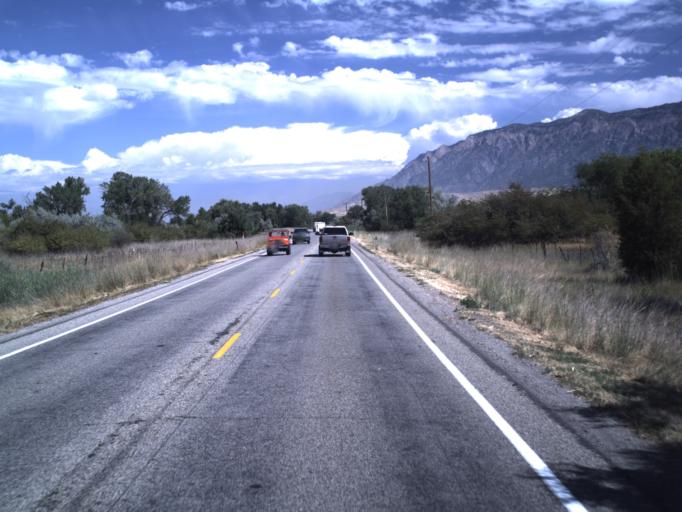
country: US
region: Utah
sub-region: Weber County
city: Marriott-Slaterville
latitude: 41.2552
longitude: -112.0251
